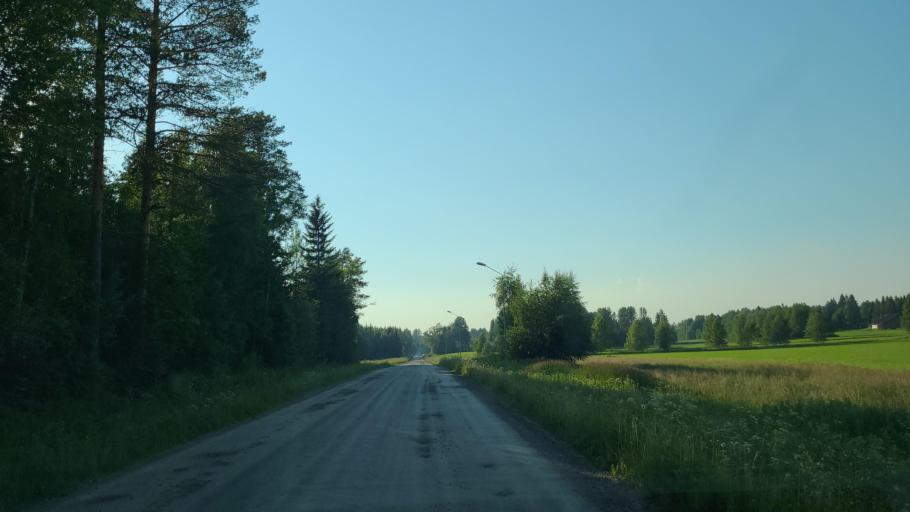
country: SE
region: Vaesterbotten
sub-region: Skelleftea Kommun
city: Burea
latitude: 64.4039
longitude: 21.3661
